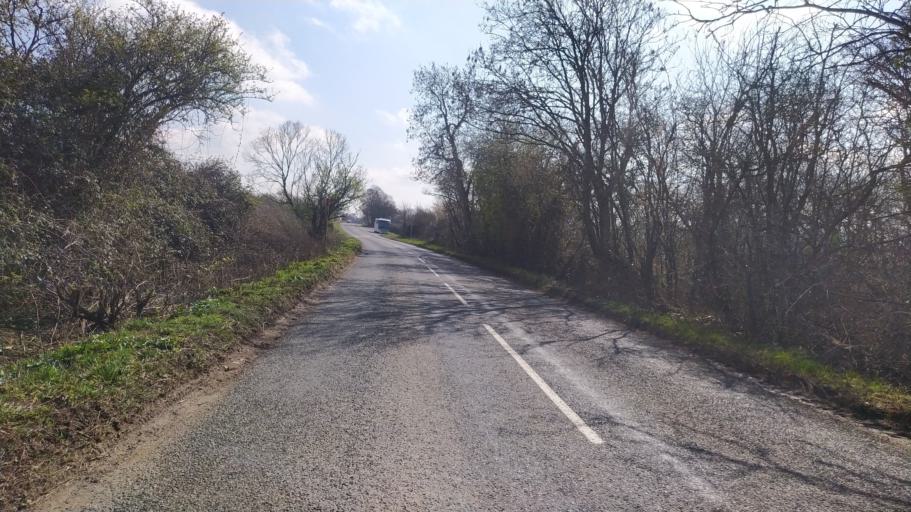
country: GB
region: England
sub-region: Somerset
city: Ilchester
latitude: 51.0163
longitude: -2.6859
